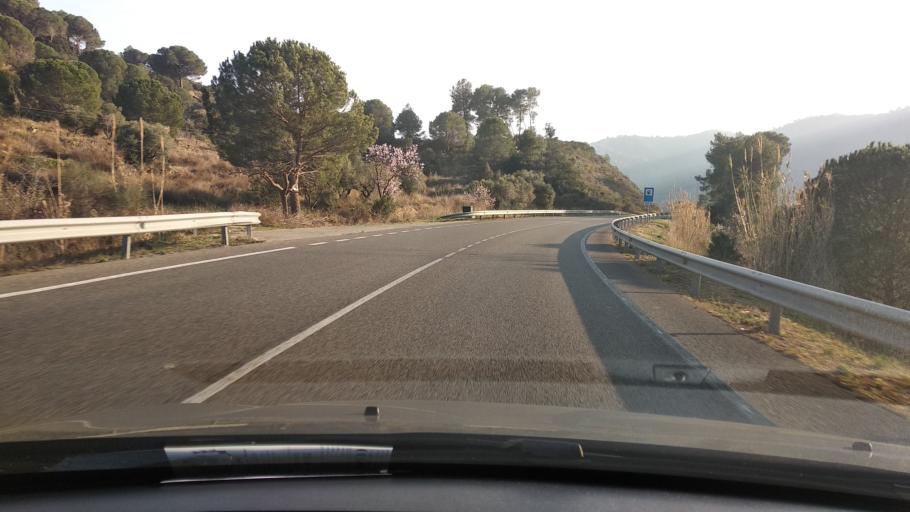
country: ES
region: Catalonia
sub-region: Provincia de Tarragona
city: Alforja
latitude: 41.1973
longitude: 0.9983
